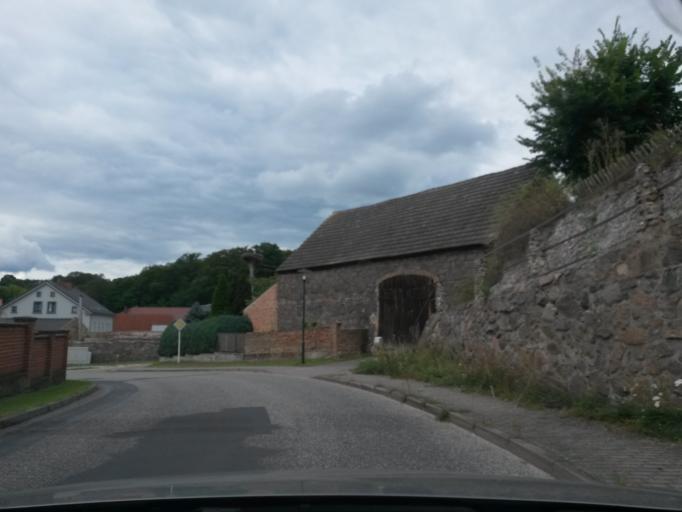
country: DE
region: Brandenburg
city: Liepe
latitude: 52.8623
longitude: 13.9725
